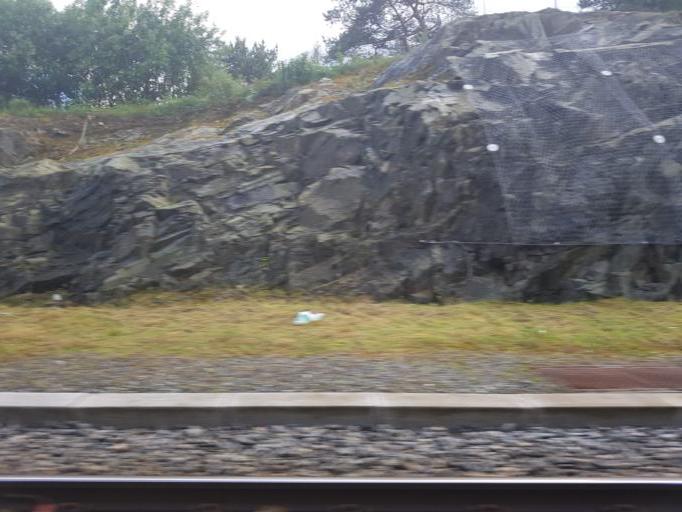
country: NO
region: Hordaland
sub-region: Bergen
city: Ytrebygda
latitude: 60.2885
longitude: 5.2567
